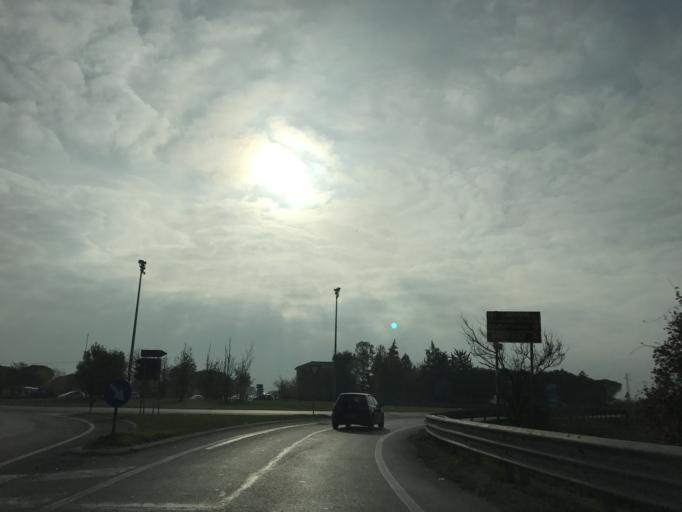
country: IT
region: Emilia-Romagna
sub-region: Provincia di Rimini
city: Santa Giustina
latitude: 44.1036
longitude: 12.4906
